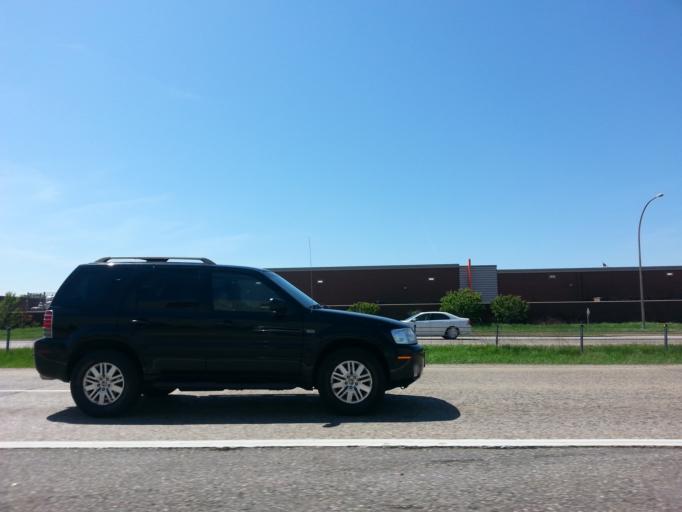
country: US
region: Minnesota
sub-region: Hennepin County
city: Richfield
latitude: 44.8870
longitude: -93.2466
